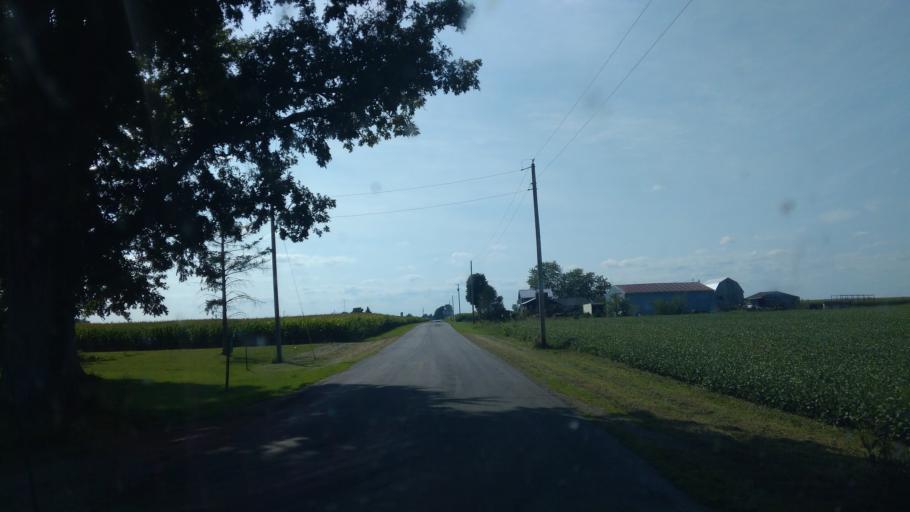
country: US
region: Ohio
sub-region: Hardin County
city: Forest
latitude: 40.6876
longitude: -83.4424
